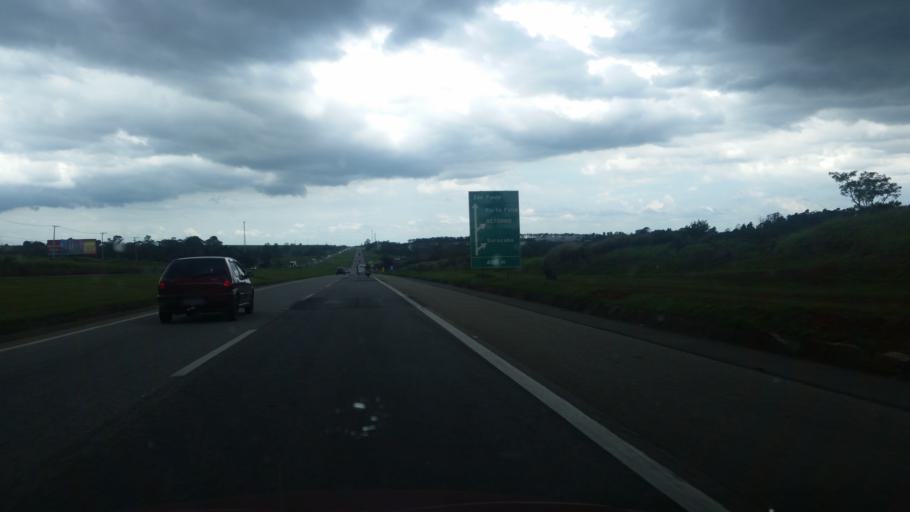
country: BR
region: Sao Paulo
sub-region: Porto Feliz
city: Porto Feliz
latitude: -23.3402
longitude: -47.5385
